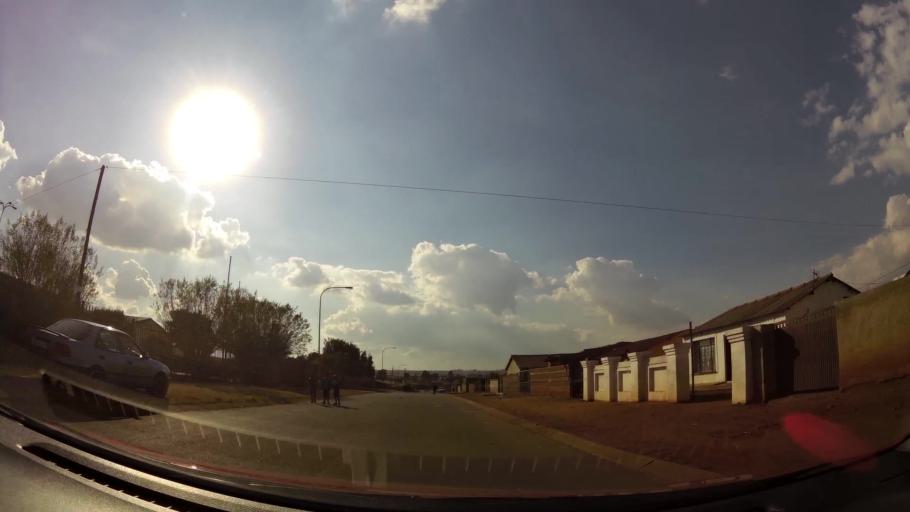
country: ZA
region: Gauteng
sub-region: City of Johannesburg Metropolitan Municipality
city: Soweto
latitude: -26.2266
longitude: 27.8676
